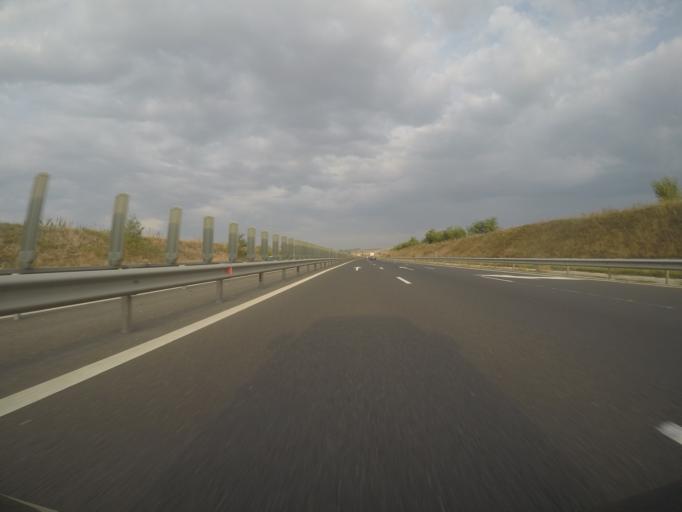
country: RO
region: Alba
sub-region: Comuna Cut
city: Cut
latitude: 45.9234
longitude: 23.6908
